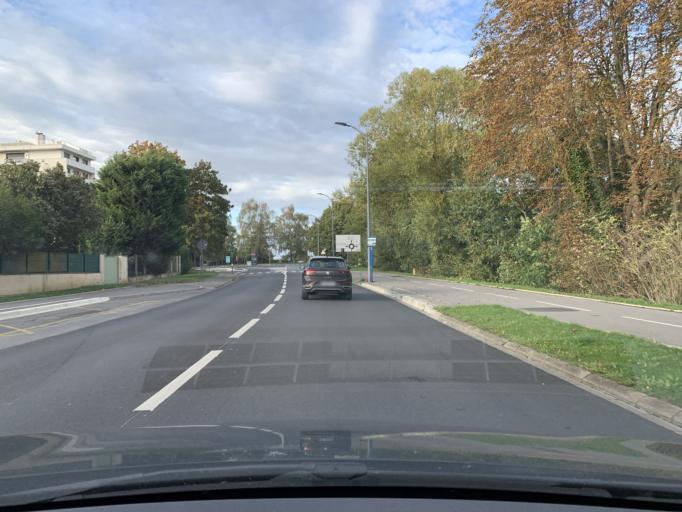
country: FR
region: Picardie
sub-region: Departement de l'Aisne
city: Harly
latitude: 49.8562
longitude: 3.3106
